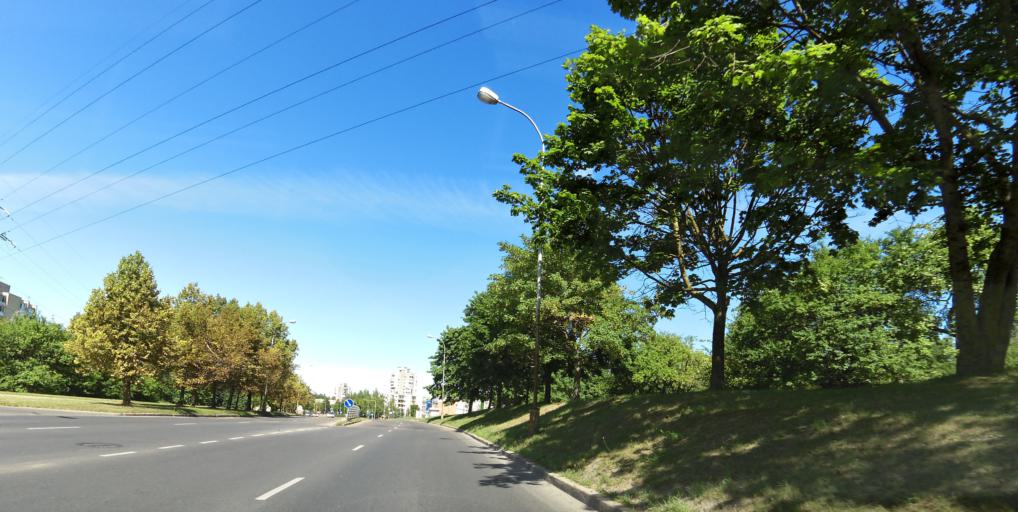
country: LT
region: Vilnius County
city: Seskine
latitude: 54.7097
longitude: 25.2402
